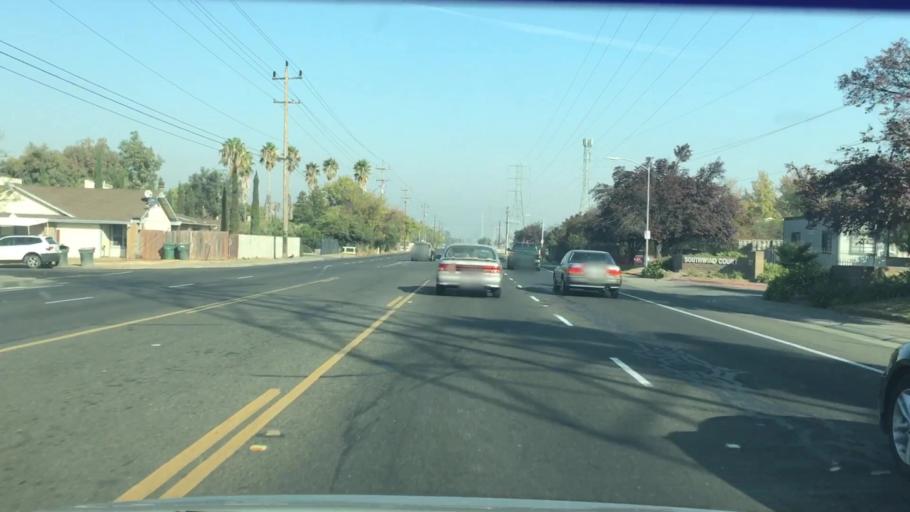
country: US
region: California
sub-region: Sacramento County
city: Florin
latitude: 38.4898
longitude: -121.4088
